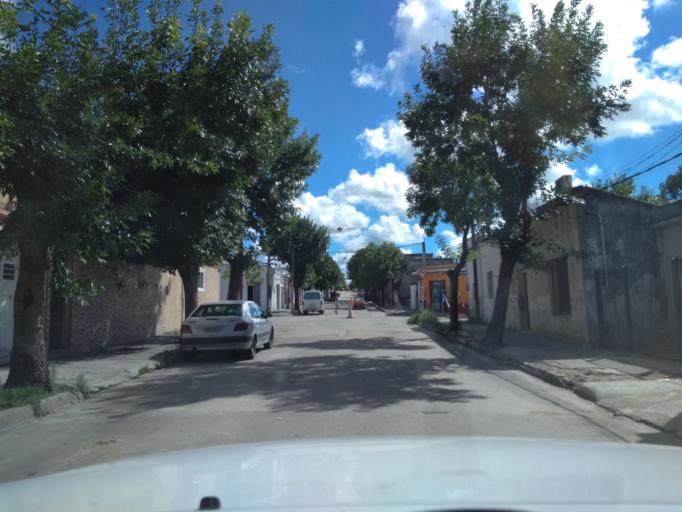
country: UY
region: Florida
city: Florida
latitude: -34.0974
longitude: -56.2100
